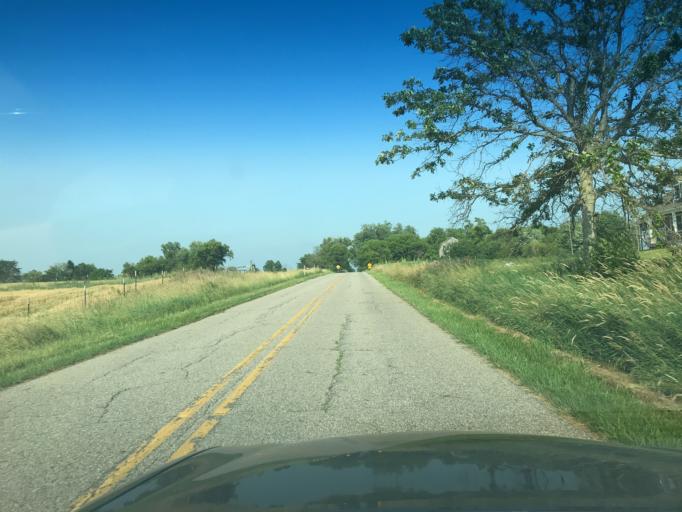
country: US
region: Michigan
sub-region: Ingham County
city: Mason
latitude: 42.5531
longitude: -84.4672
